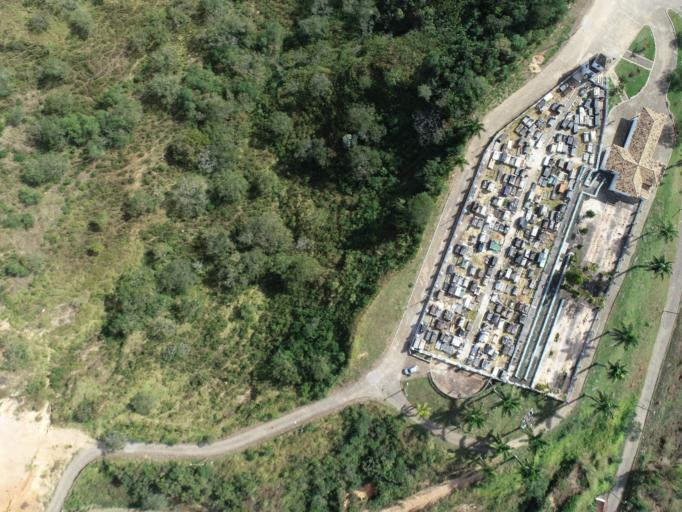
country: BR
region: Minas Gerais
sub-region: Tiradentes
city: Tiradentes
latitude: -21.0569
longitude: -44.0836
